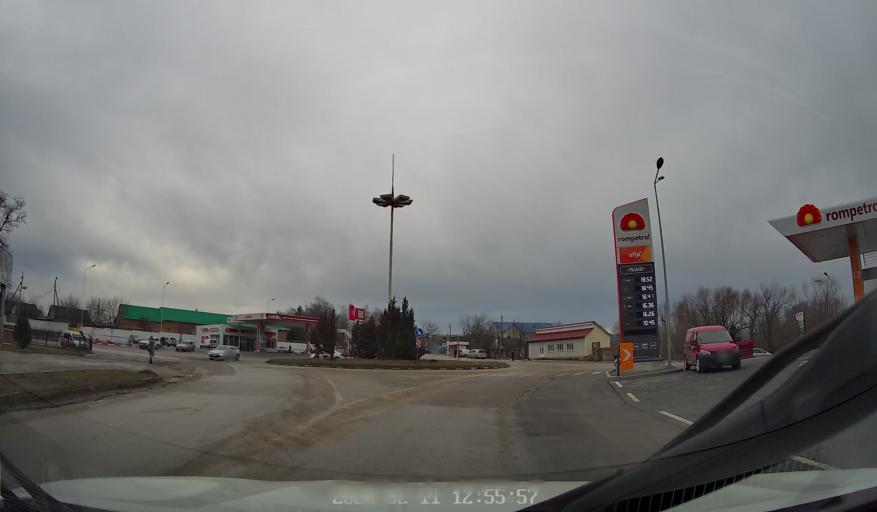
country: MD
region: Briceni
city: Briceni
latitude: 48.3507
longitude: 27.0849
